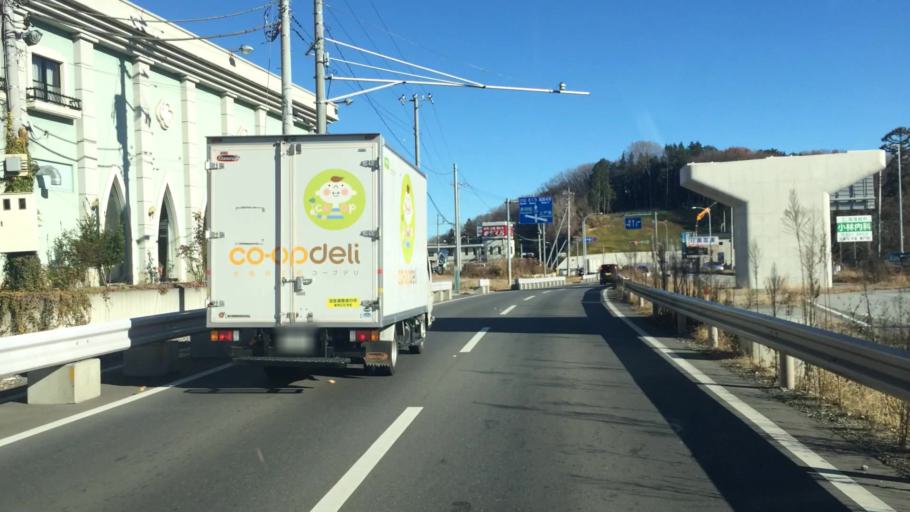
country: JP
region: Tochigi
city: Utsunomiya-shi
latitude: 36.5931
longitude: 139.8694
